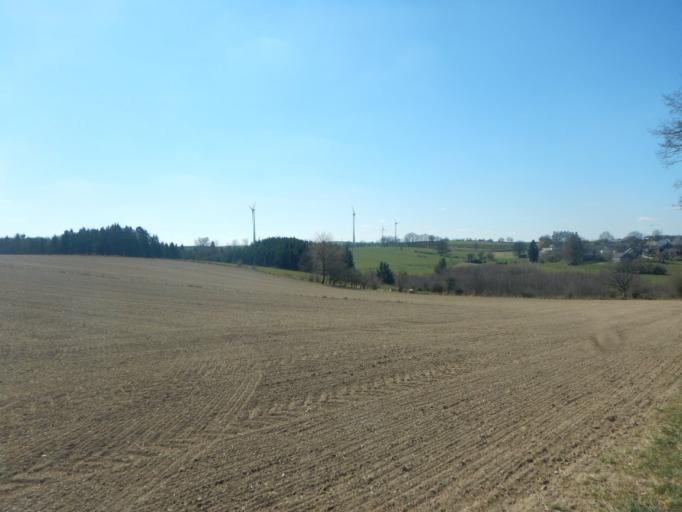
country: LU
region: Diekirch
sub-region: Canton de Clervaux
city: Weiswampach
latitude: 50.1184
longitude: 6.0460
